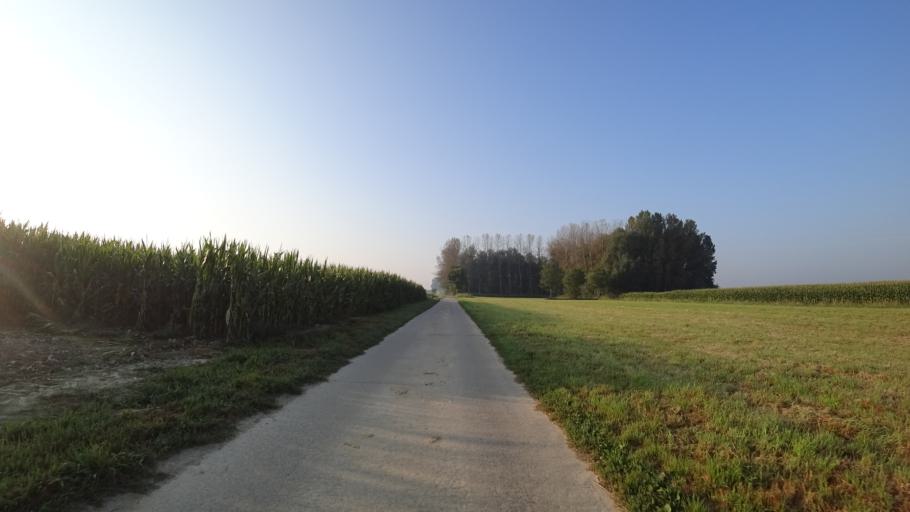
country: BE
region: Wallonia
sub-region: Province du Brabant Wallon
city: Walhain-Saint-Paul
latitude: 50.6275
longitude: 4.6763
